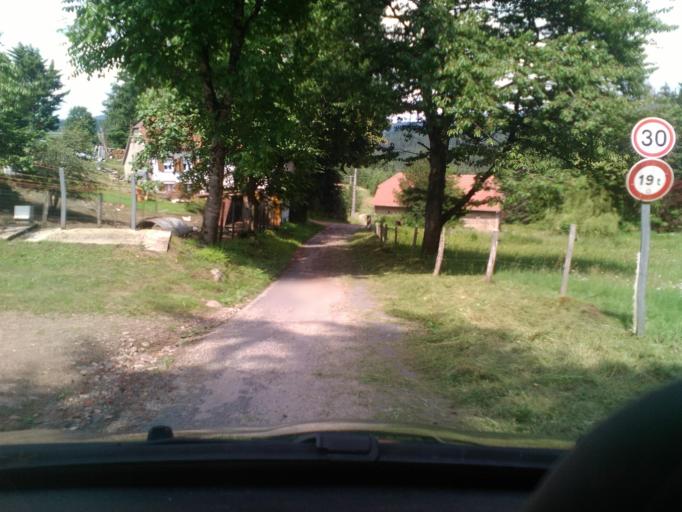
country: FR
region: Lorraine
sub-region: Departement des Vosges
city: Senones
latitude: 48.3727
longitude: 7.0449
